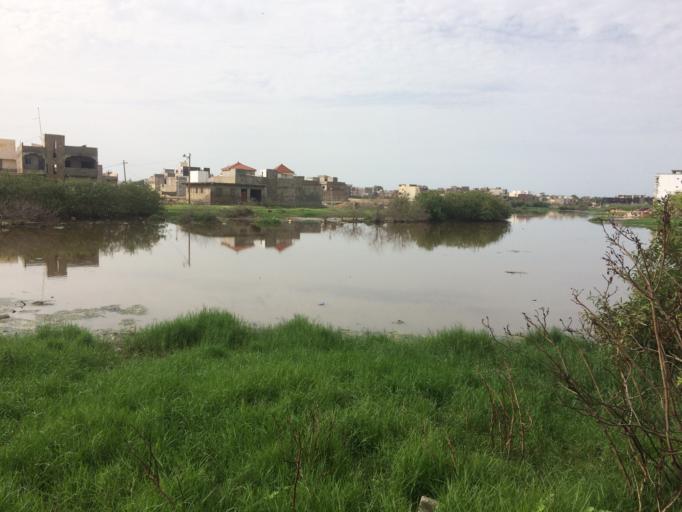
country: SN
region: Dakar
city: Pikine
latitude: 14.7389
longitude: -17.3247
